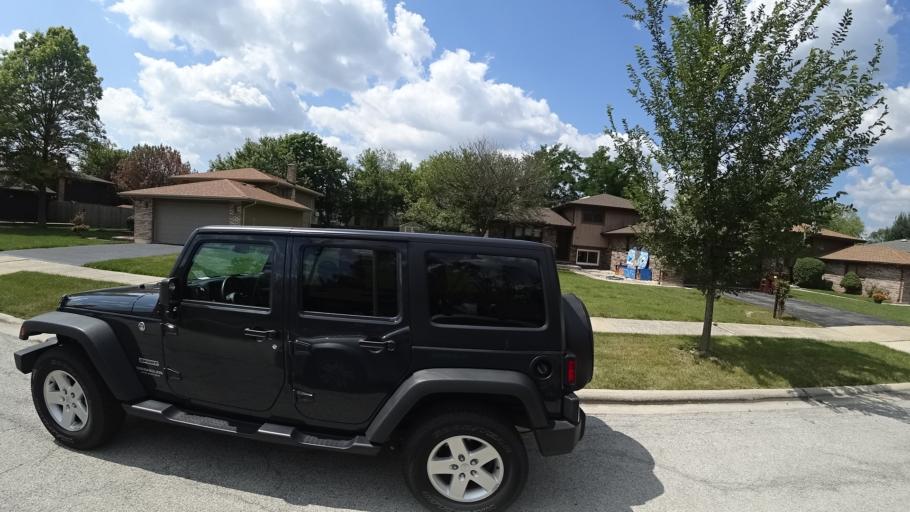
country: US
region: Illinois
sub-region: Cook County
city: Oak Forest
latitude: 41.6252
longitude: -87.7819
